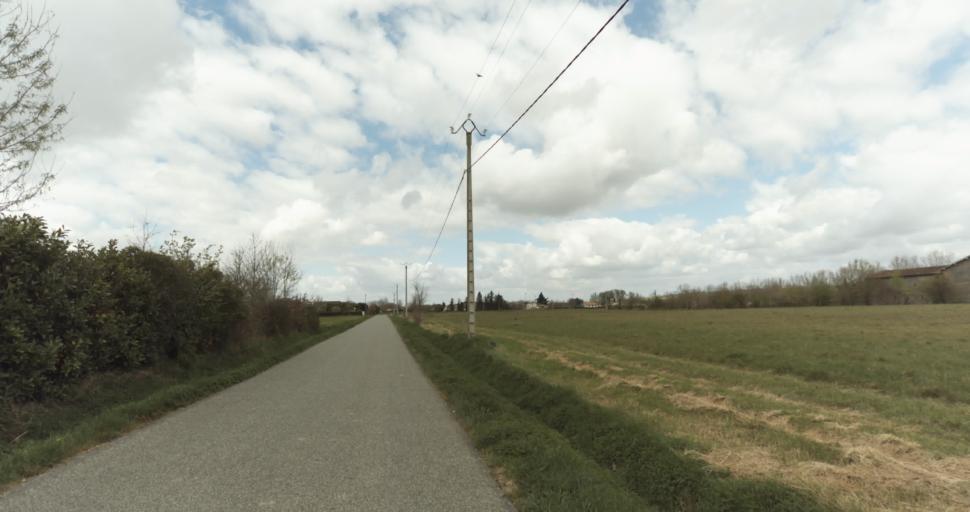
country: FR
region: Midi-Pyrenees
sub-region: Departement de la Haute-Garonne
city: Auterive
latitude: 43.3381
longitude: 1.4719
